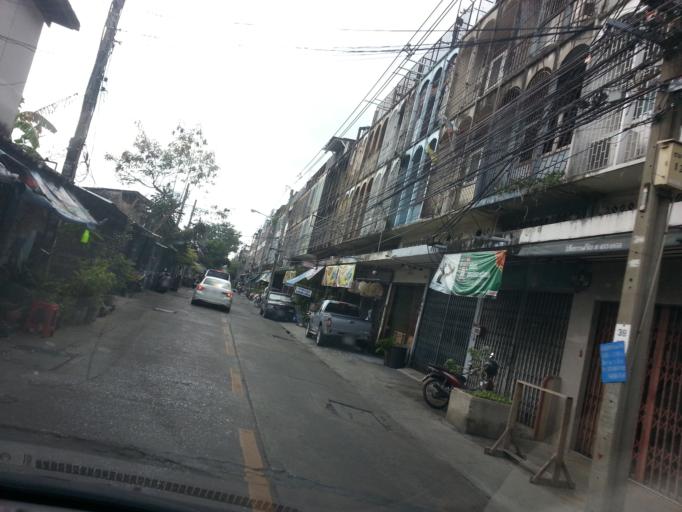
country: TH
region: Bangkok
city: Khlong Toei
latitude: 13.7140
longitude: 100.5736
